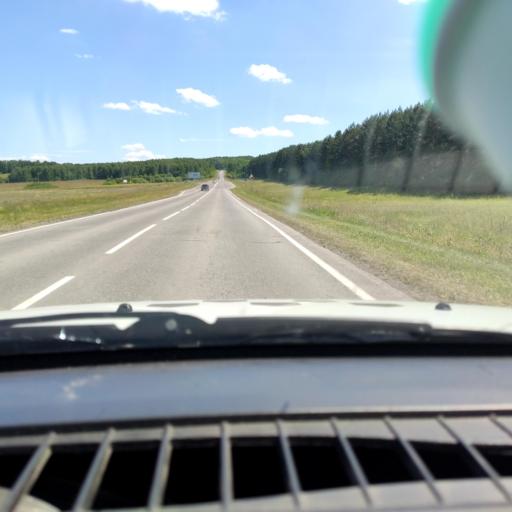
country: RU
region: Bashkortostan
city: Verkhniye Kigi
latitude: 55.3915
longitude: 58.6537
